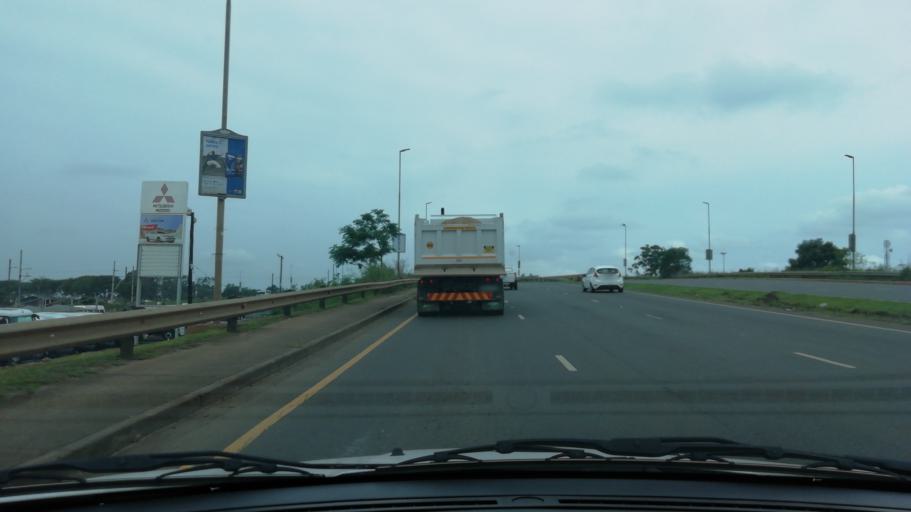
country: ZA
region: KwaZulu-Natal
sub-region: uThungulu District Municipality
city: Empangeni
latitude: -28.7658
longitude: 31.9101
